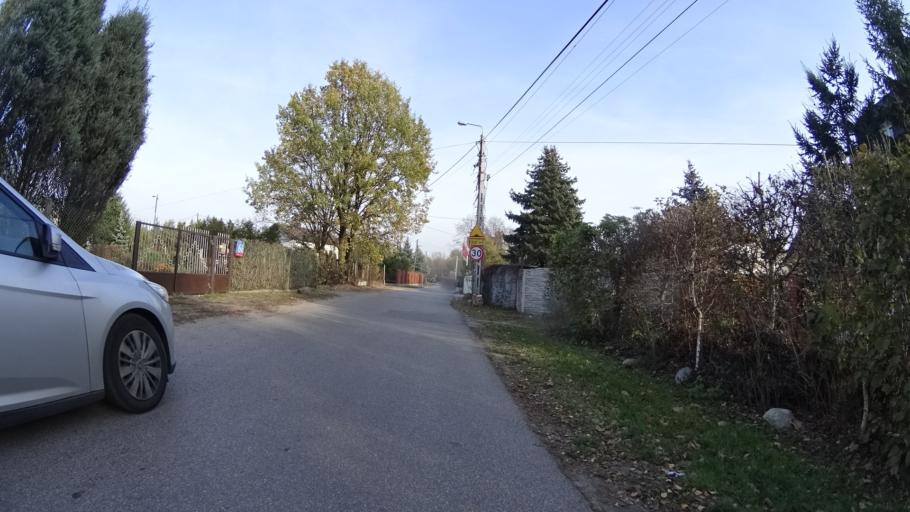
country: PL
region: Masovian Voivodeship
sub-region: Powiat warszawski zachodni
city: Lomianki
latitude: 52.2943
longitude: 20.8801
